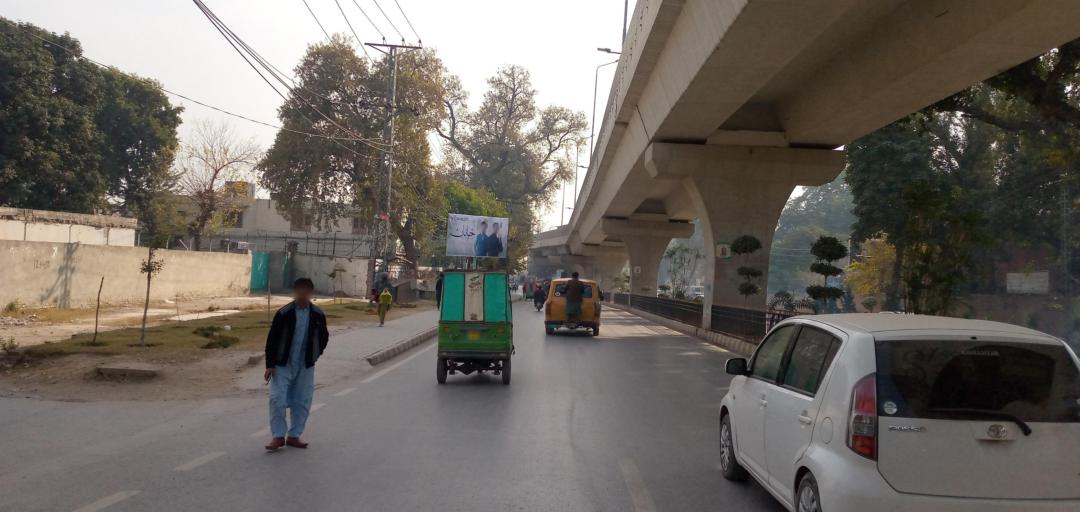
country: PK
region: Khyber Pakhtunkhwa
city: Peshawar
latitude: 34.0001
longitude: 71.5320
